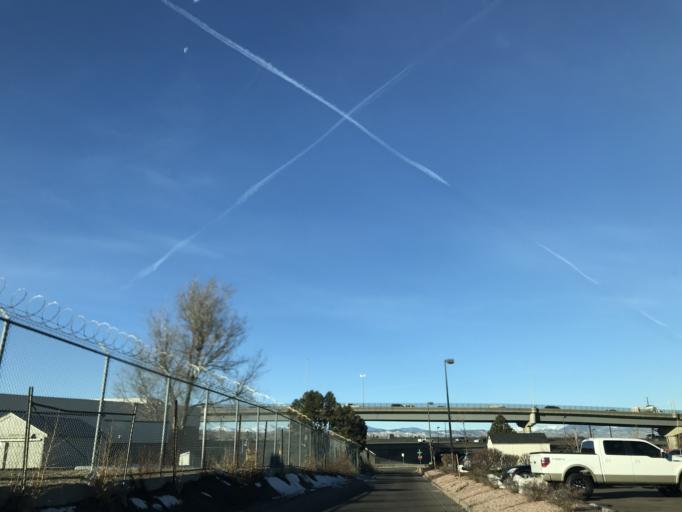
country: US
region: Colorado
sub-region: Denver County
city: Denver
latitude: 39.7058
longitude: -104.9936
